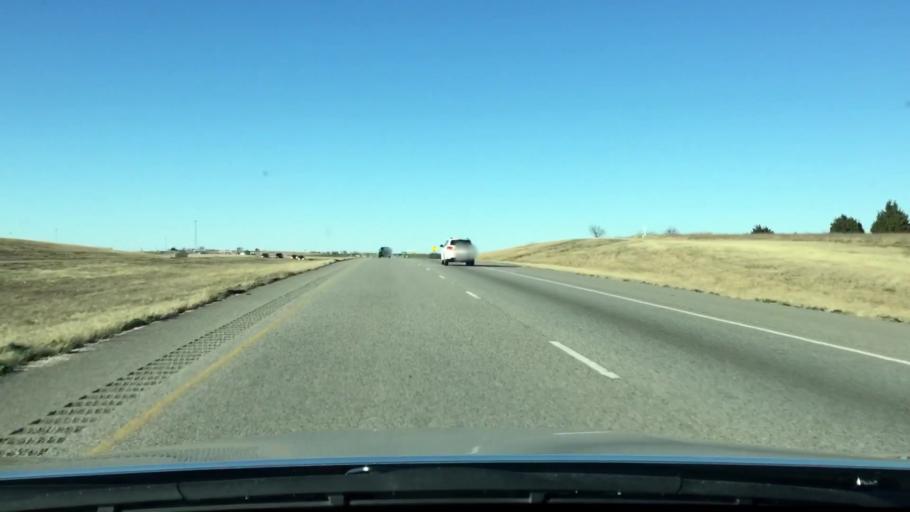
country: US
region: Texas
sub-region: Hill County
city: Itasca
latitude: 32.1411
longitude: -97.1224
